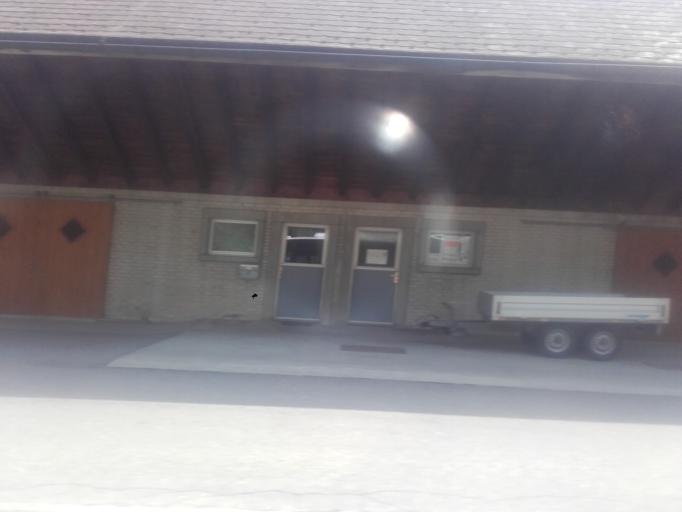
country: CH
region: Solothurn
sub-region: Bezirk Thal
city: Welschenrohr
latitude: 47.2643
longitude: 7.4759
